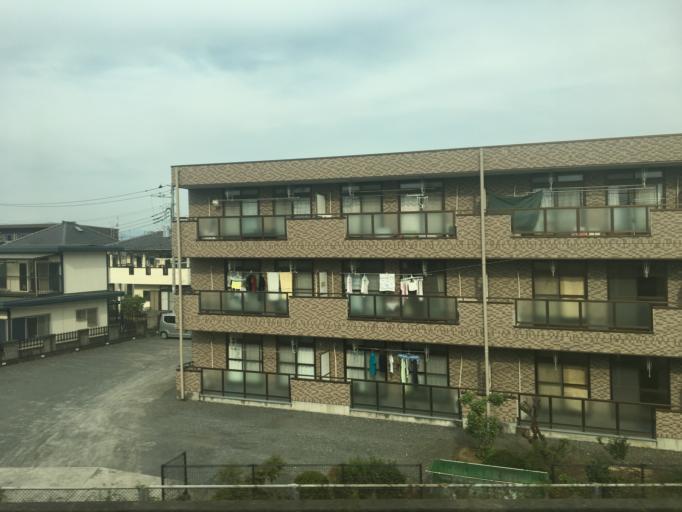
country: JP
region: Saitama
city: Sayama
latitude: 35.8624
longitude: 139.4182
